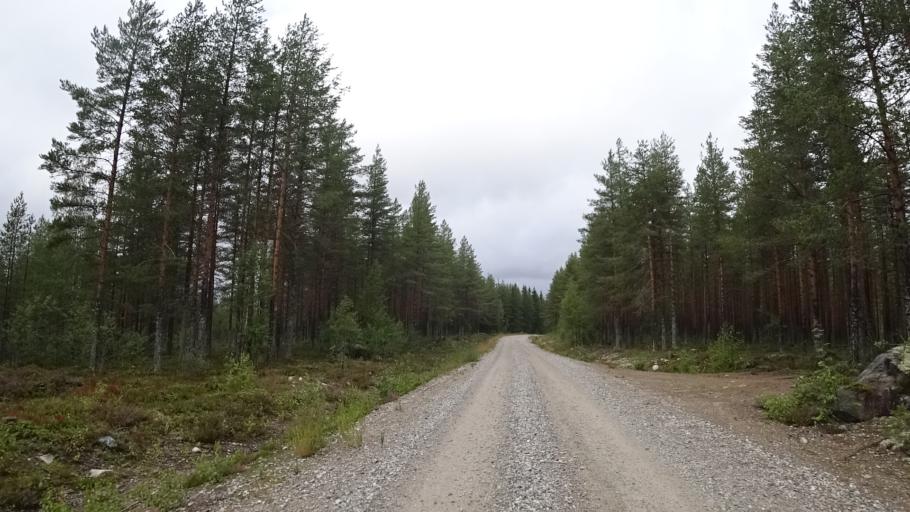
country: FI
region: North Karelia
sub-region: Pielisen Karjala
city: Lieksa
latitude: 63.4740
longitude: 30.2669
